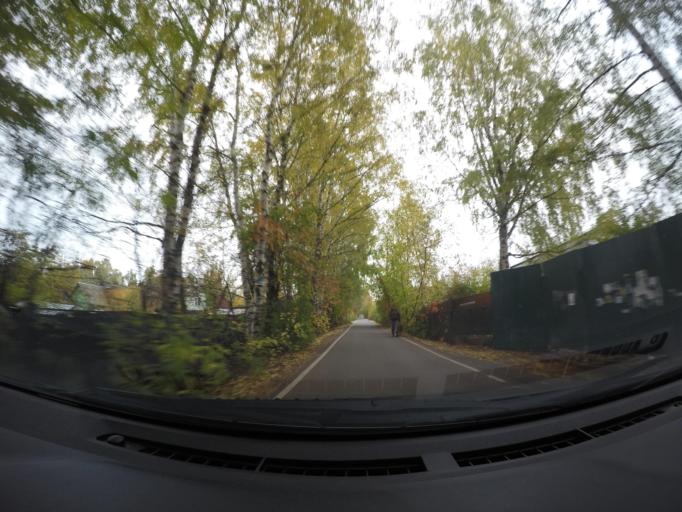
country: RU
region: Moskovskaya
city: Imeni Vorovskogo
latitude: 55.7323
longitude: 38.3069
